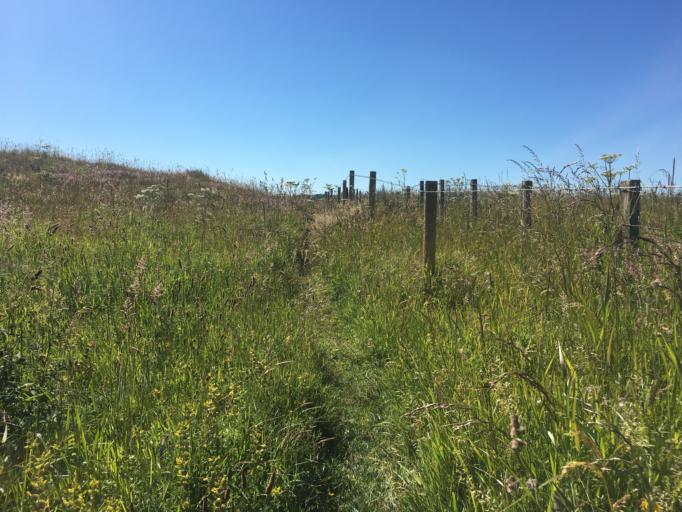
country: GB
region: England
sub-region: Northumberland
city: Beadnell
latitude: 55.5444
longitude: -1.6381
